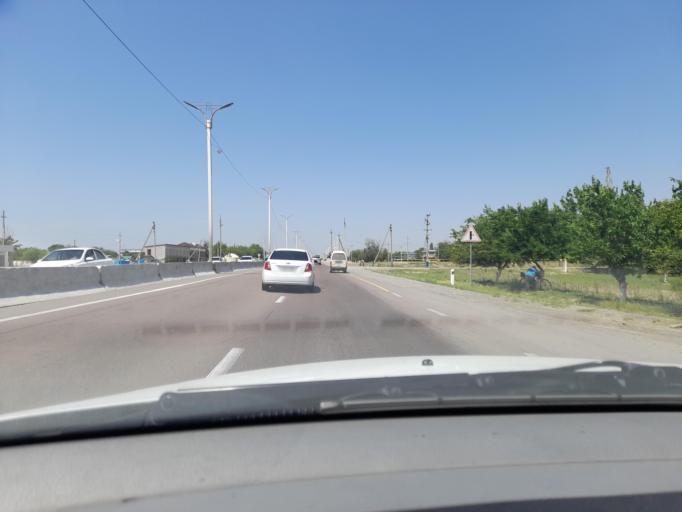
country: KZ
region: Ongtustik Qazaqstan
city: Myrzakent
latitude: 40.5386
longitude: 68.4242
